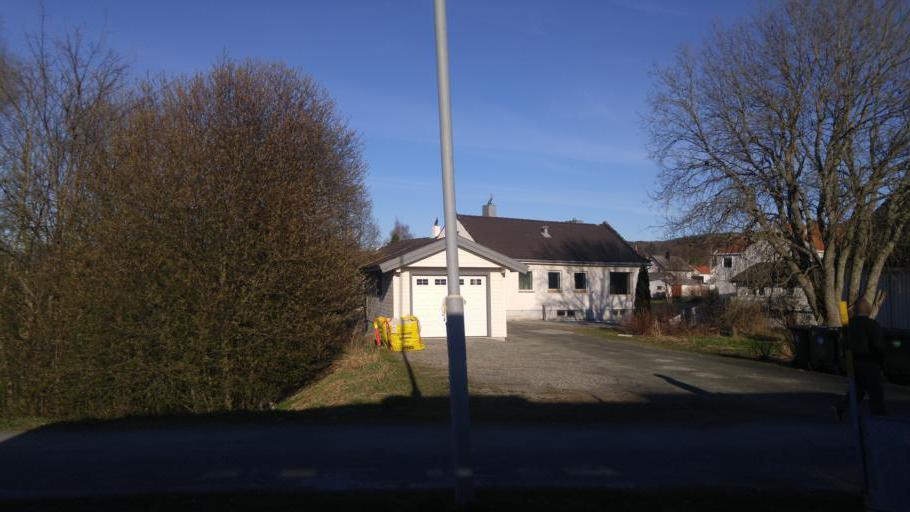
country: NO
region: Sor-Trondelag
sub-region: Trondheim
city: Trondheim
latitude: 63.4145
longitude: 10.4452
